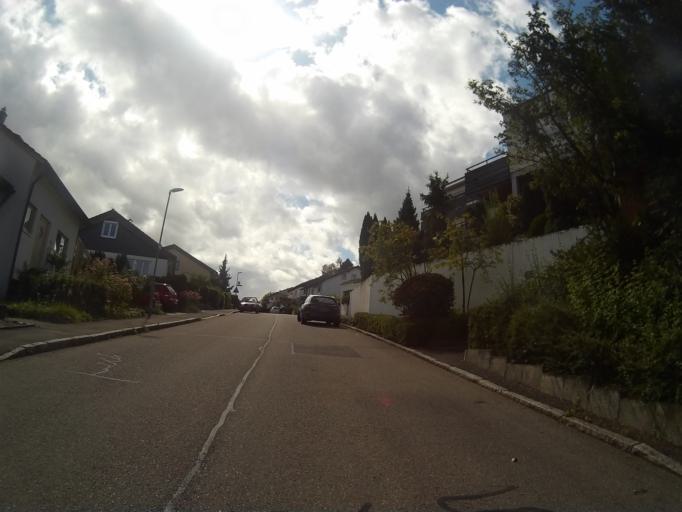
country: DE
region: Baden-Wuerttemberg
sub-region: Tuebingen Region
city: Pfullingen
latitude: 48.4703
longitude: 9.2184
